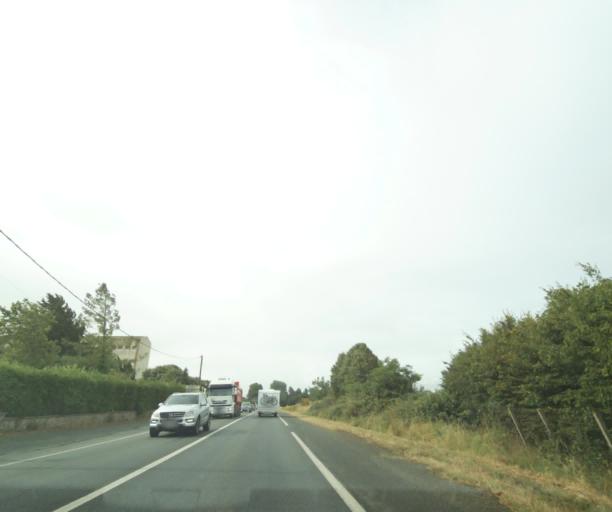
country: FR
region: Pays de la Loire
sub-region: Departement de la Vendee
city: Sainte-Gemme-la-Plaine
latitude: 46.4506
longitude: -1.1038
